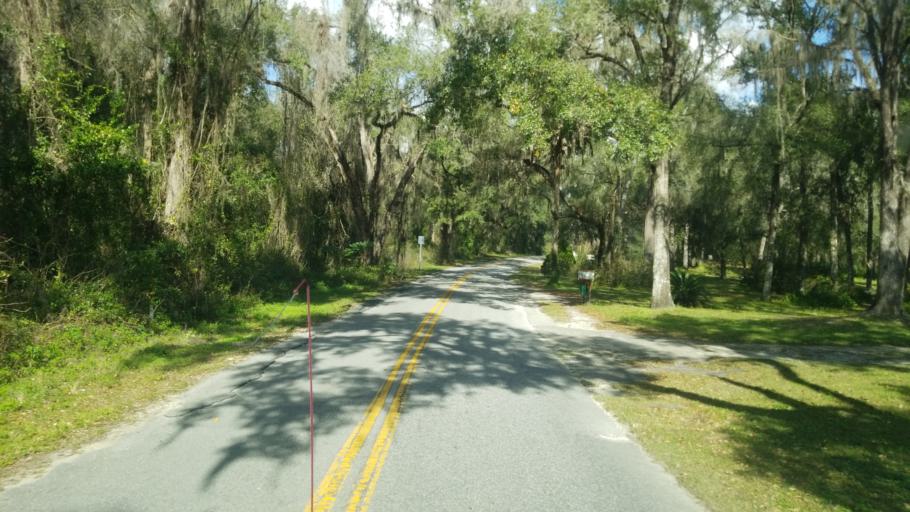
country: US
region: Florida
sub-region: Citrus County
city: Floral City
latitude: 28.7286
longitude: -82.2980
